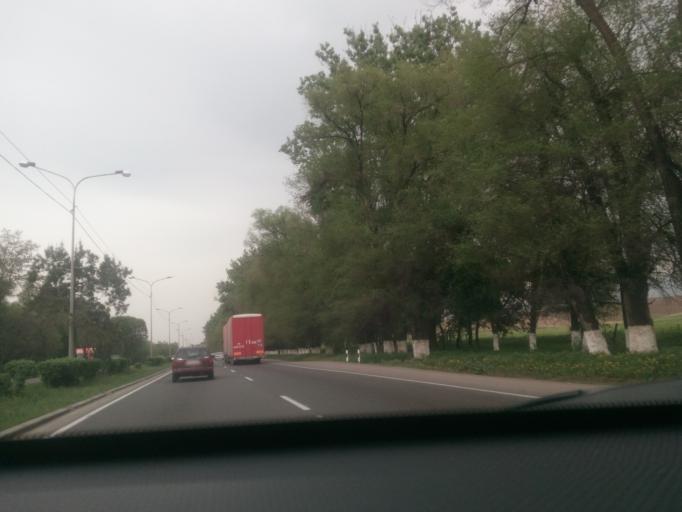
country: KZ
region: Almaty Oblysy
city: Burunday
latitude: 43.2197
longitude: 76.7114
